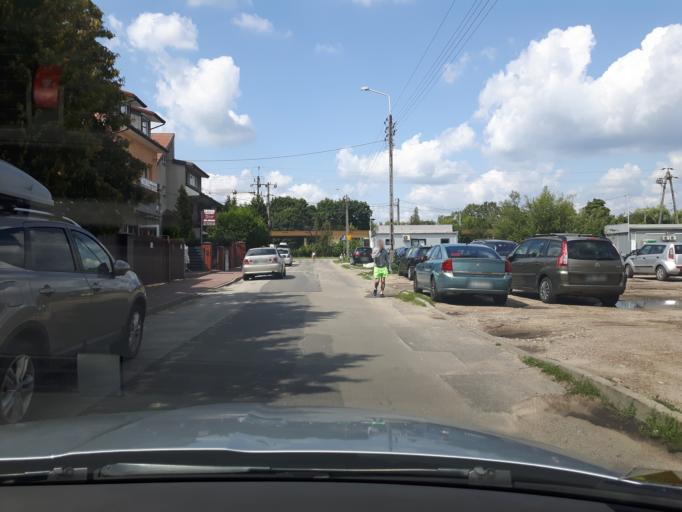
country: PL
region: Masovian Voivodeship
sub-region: Powiat wolominski
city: Zabki
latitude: 52.2916
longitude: 21.1143
